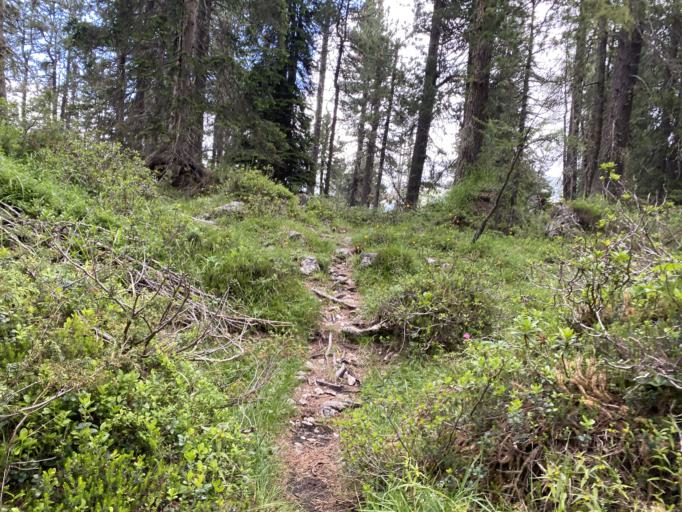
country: IT
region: Trentino-Alto Adige
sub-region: Bolzano
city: Selva
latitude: 46.6229
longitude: 11.7736
